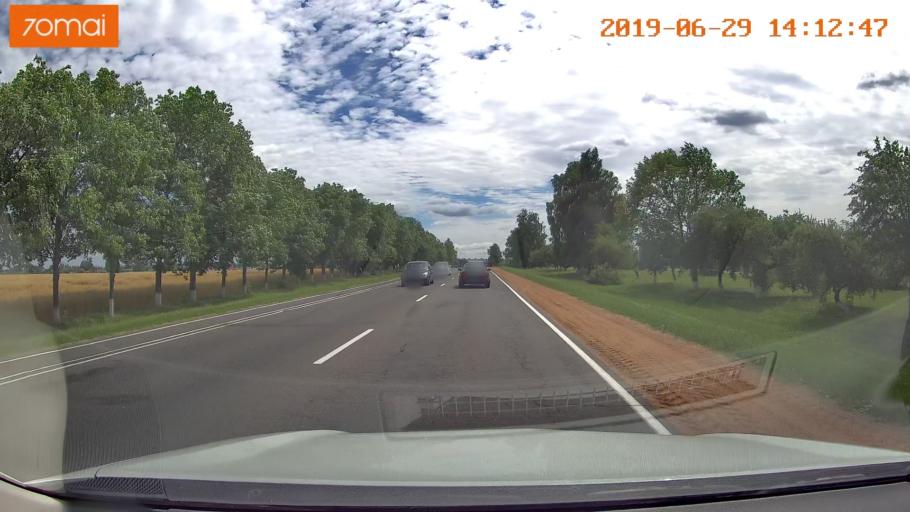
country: BY
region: Minsk
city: Salihorsk
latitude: 52.8073
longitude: 27.5087
